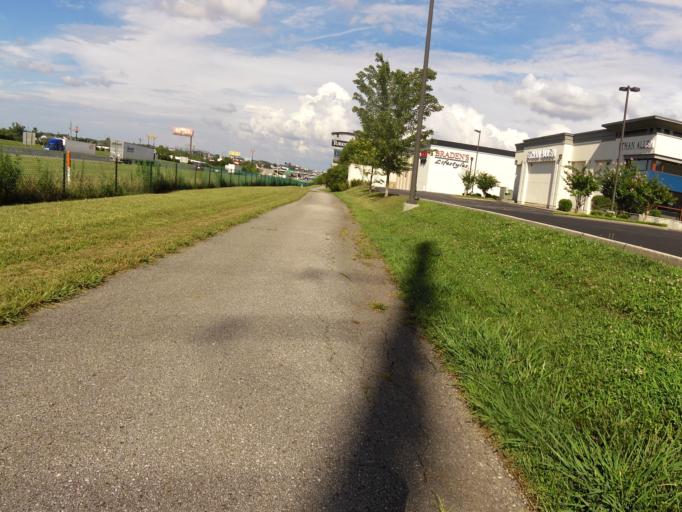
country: US
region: Tennessee
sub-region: Knox County
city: Farragut
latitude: 35.9034
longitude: -84.1540
